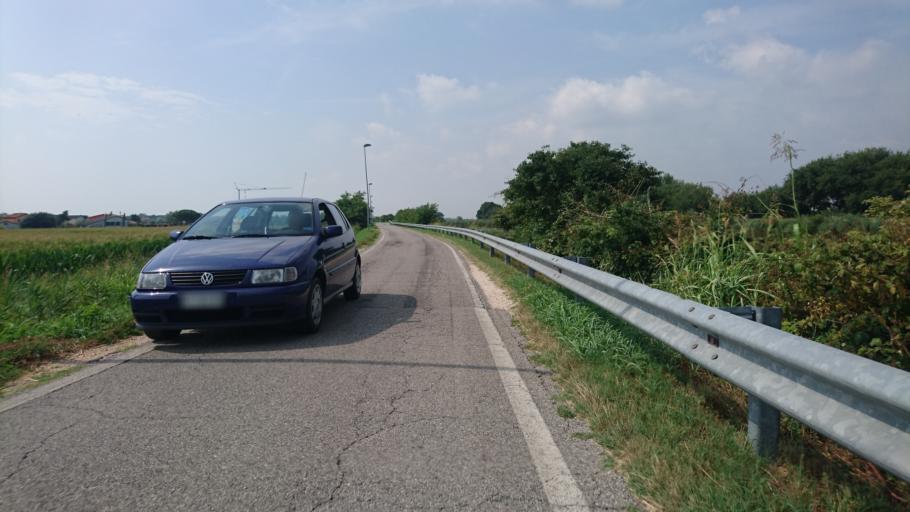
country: IT
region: Veneto
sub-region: Provincia di Venezia
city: Sant'Anna
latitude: 45.1440
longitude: 12.2589
